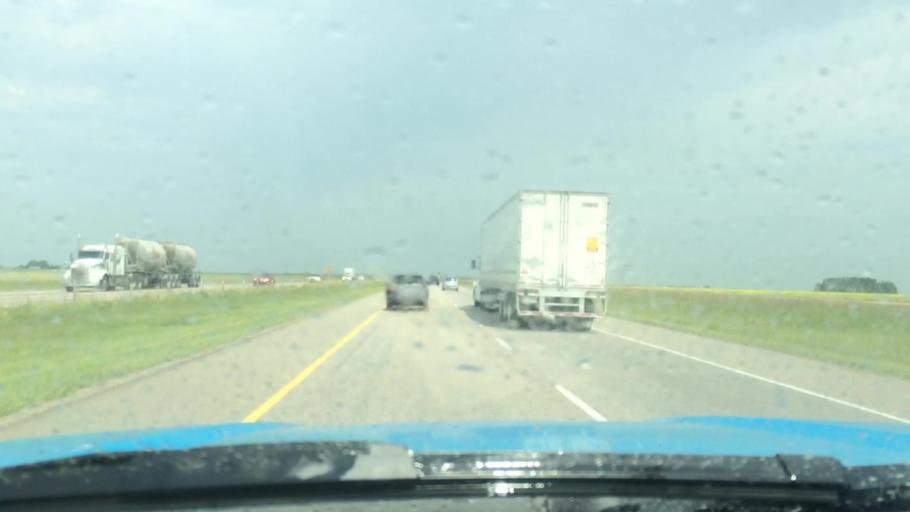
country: CA
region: Alberta
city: Didsbury
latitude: 51.6523
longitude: -114.0254
